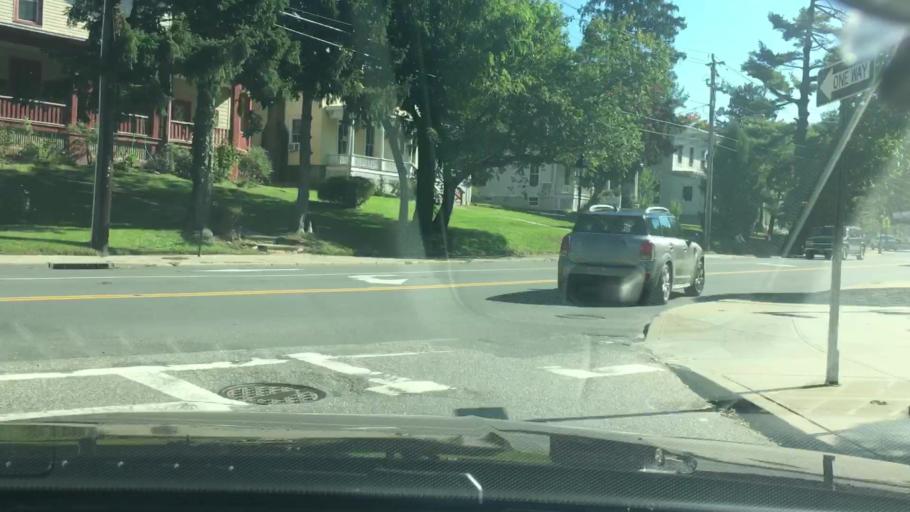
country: US
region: New York
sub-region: Suffolk County
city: Port Jefferson
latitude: 40.9417
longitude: -73.0665
